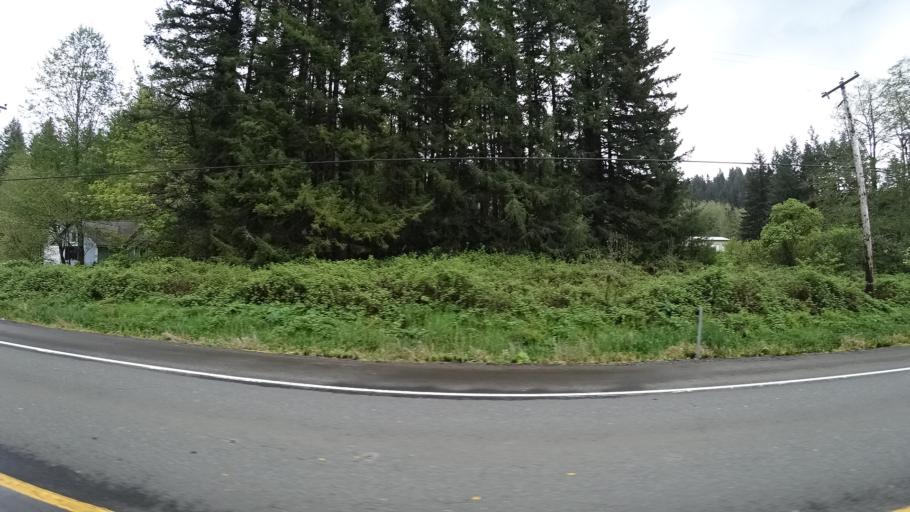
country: US
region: Oregon
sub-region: Lincoln County
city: Rose Lodge
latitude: 45.0162
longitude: -123.8720
